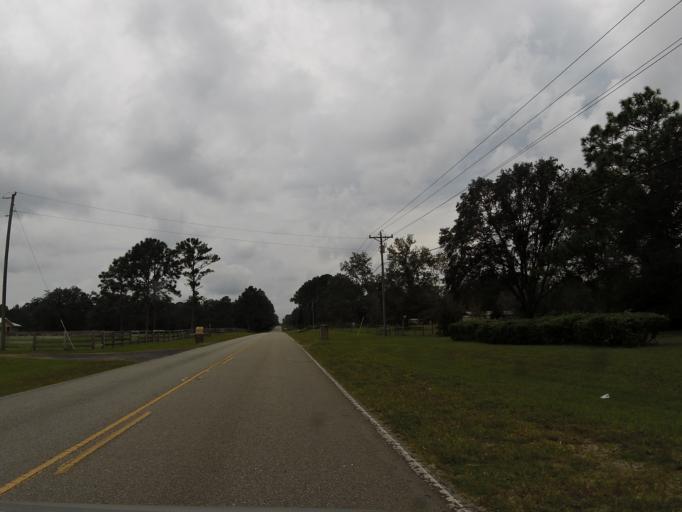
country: US
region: Florida
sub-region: Clay County
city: Middleburg
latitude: 30.1165
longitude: -81.9491
